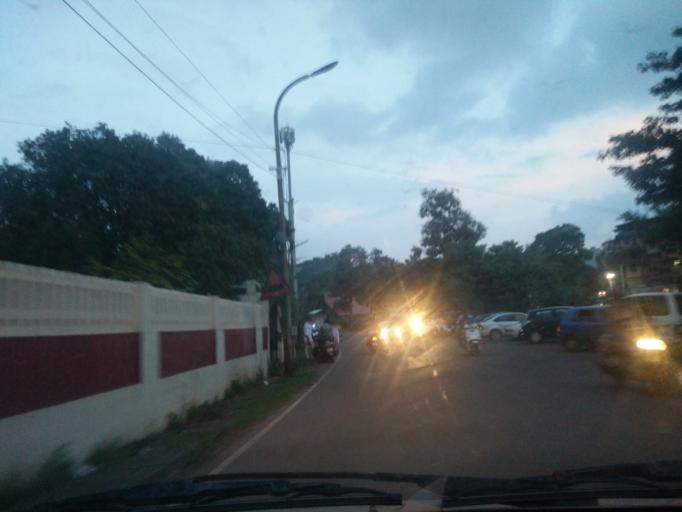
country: IN
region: Goa
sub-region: South Goa
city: Madgaon
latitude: 15.2781
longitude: 73.9612
